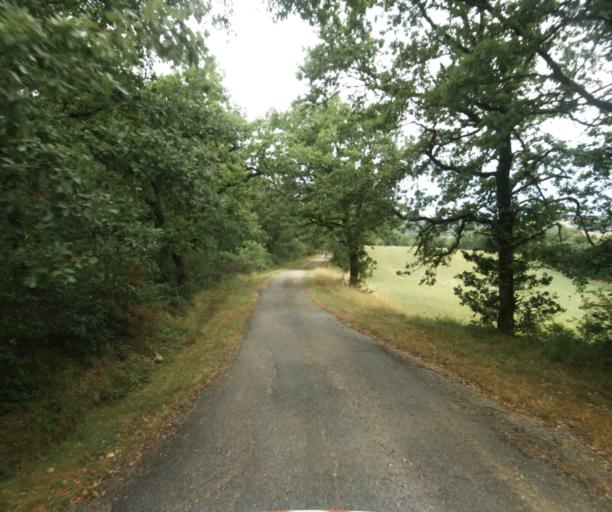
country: FR
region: Midi-Pyrenees
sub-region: Departement de la Haute-Garonne
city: Revel
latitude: 43.4135
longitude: 1.9823
